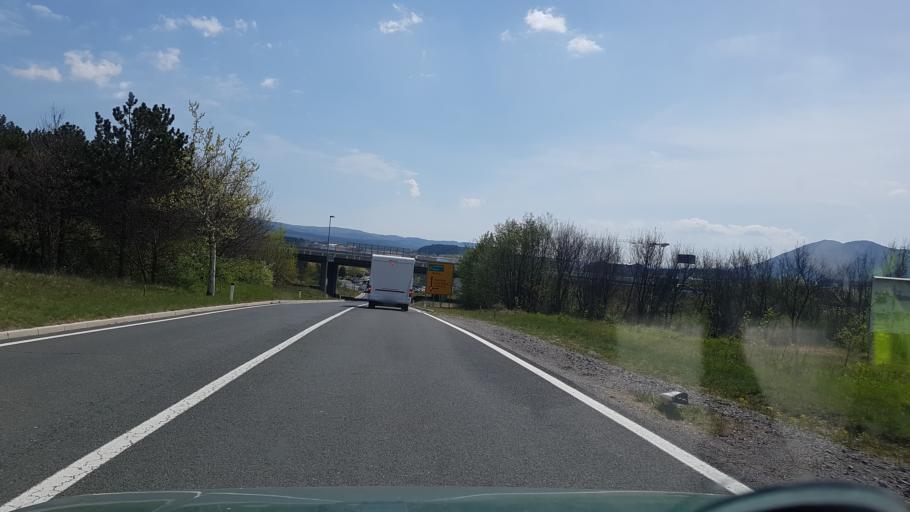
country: SI
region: Hrpelje-Kozina
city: Kozina
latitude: 45.6095
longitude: 13.9280
